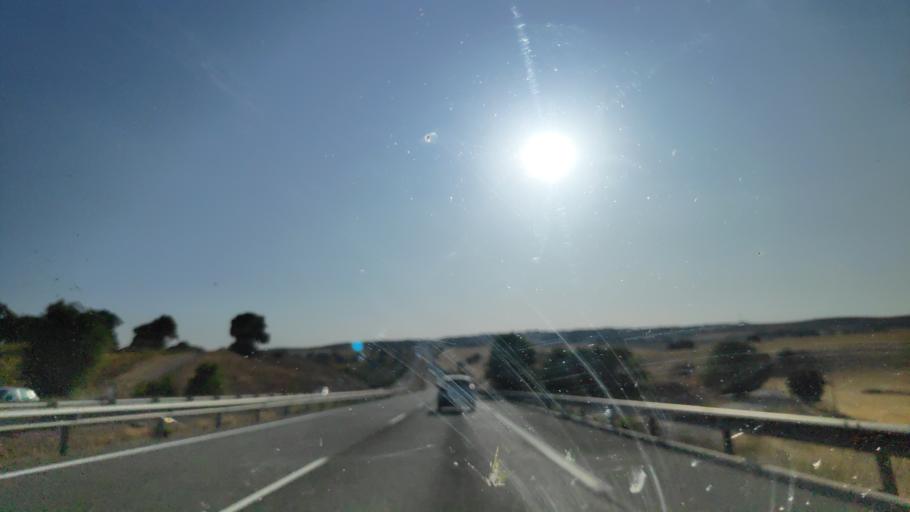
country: ES
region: Castille-La Mancha
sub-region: Provincia de Cuenca
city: Saelices
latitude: 39.9150
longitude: -2.7687
